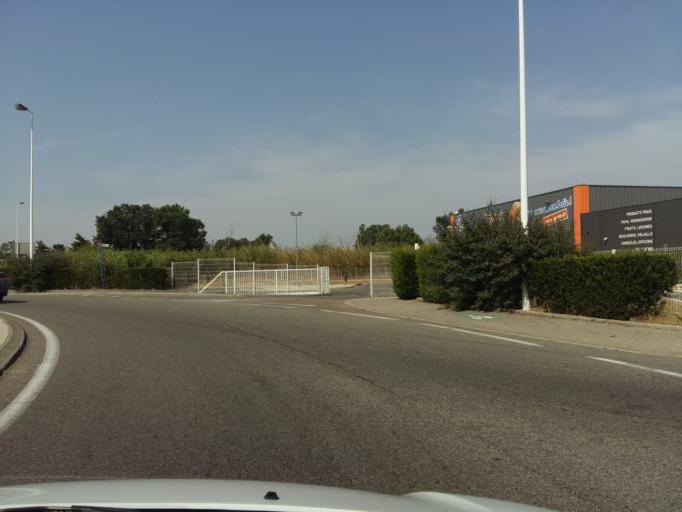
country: FR
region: Rhone-Alpes
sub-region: Departement de la Drome
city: Saint-Paul-Trois-Chateaux
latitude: 44.3241
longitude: 4.7414
